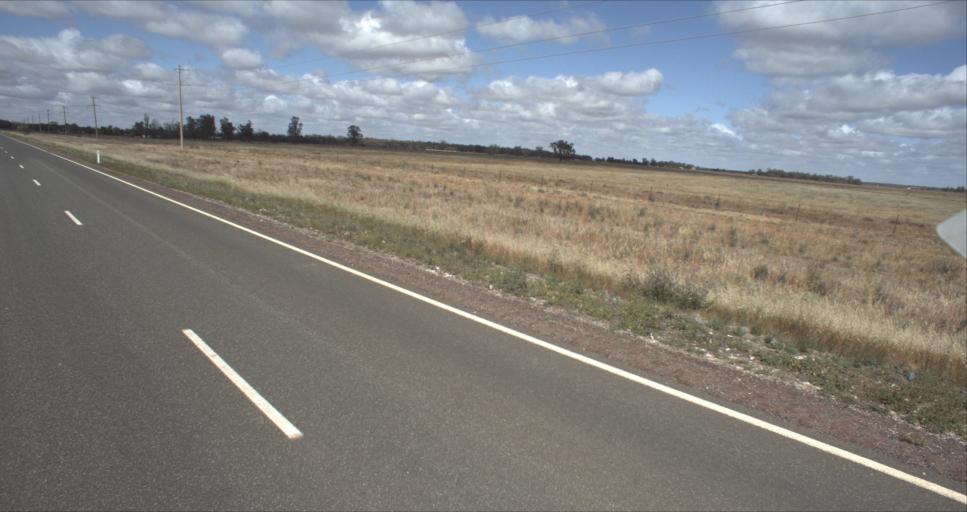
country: AU
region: New South Wales
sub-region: Murrumbidgee Shire
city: Darlington Point
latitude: -34.5870
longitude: 146.1641
